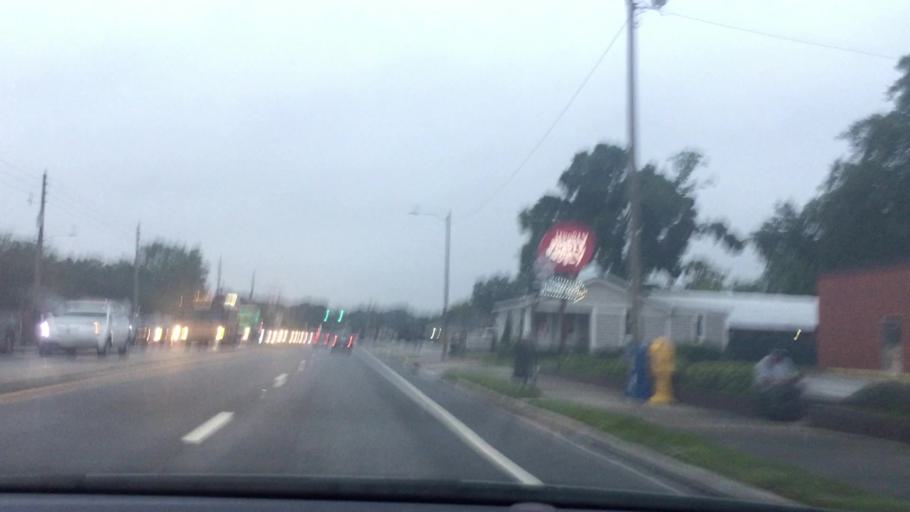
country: US
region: Florida
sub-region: Orange County
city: Fairview Shores
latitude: 28.5825
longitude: -81.3900
